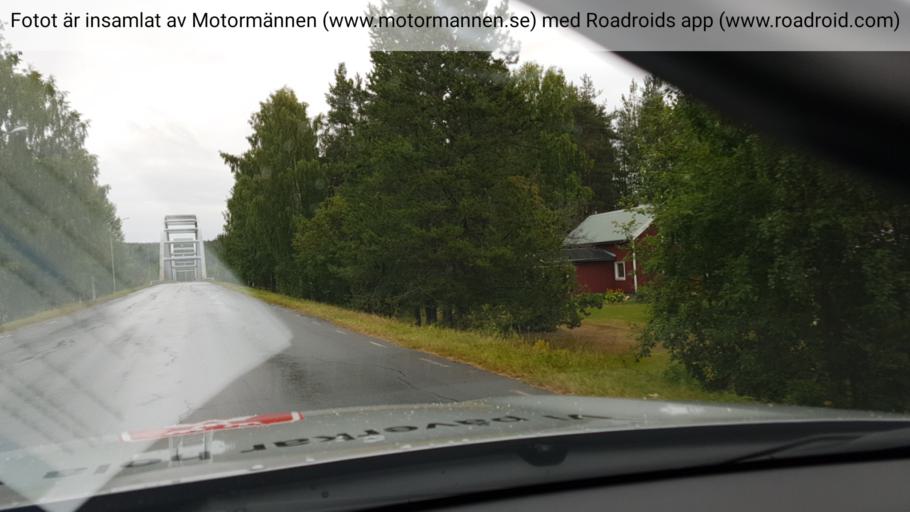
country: SE
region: Norrbotten
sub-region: Alvsbyns Kommun
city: AElvsbyn
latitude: 66.0905
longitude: 20.9176
